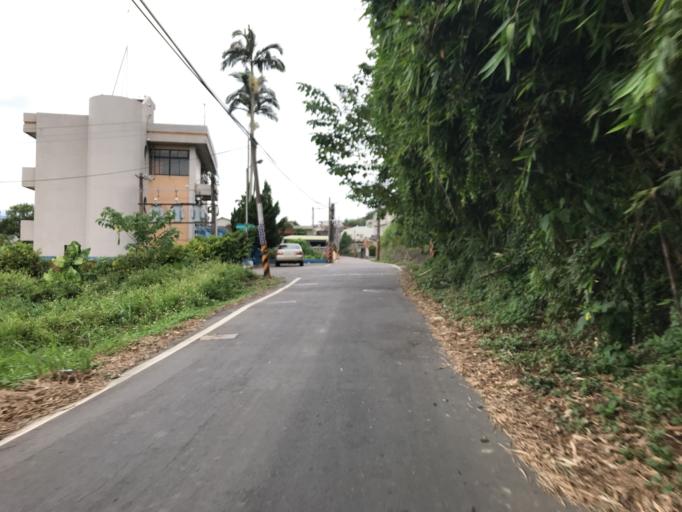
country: TW
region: Taiwan
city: Daxi
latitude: 24.7835
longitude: 121.1755
